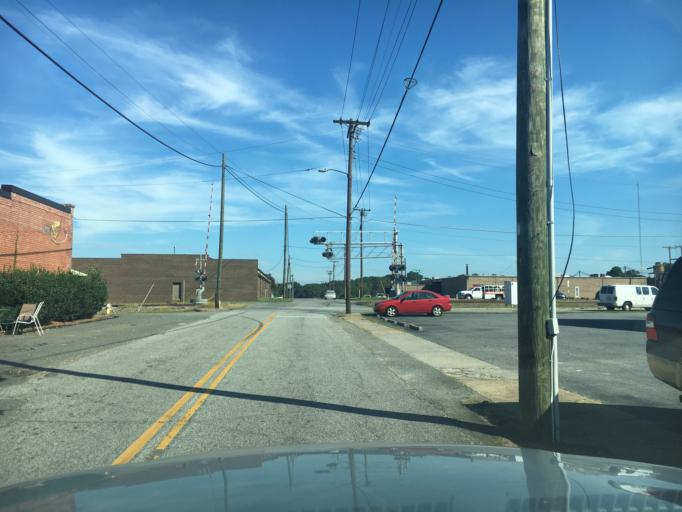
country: US
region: North Carolina
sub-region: Catawba County
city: Hickory
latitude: 35.7313
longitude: -81.3524
